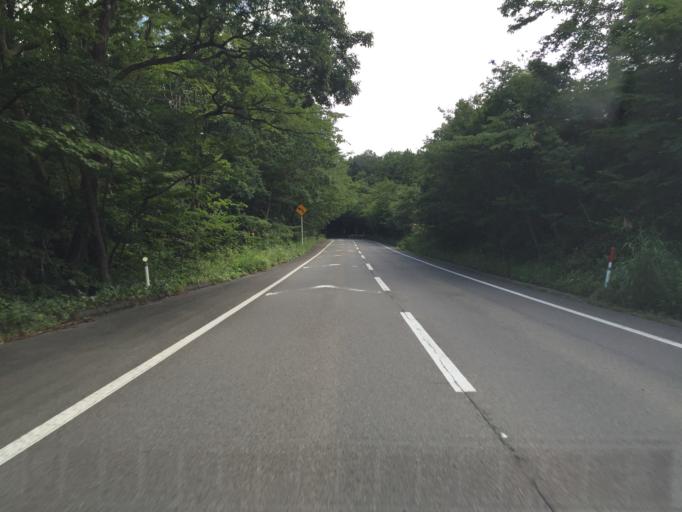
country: JP
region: Fukushima
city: Nihommatsu
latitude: 37.6362
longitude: 140.3462
